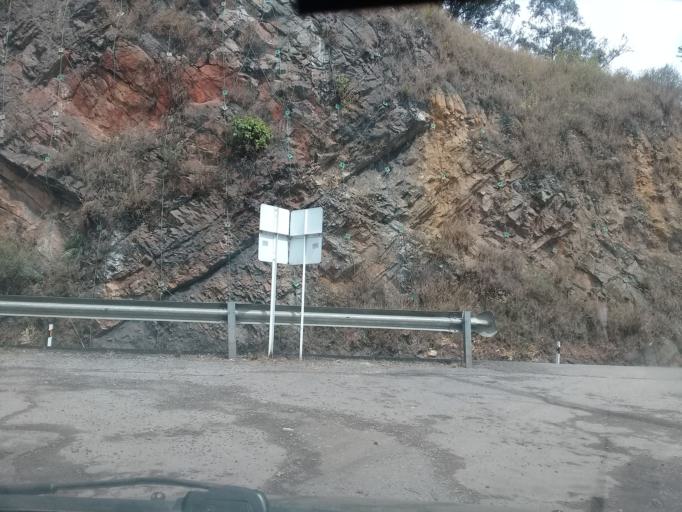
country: CO
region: Cundinamarca
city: Une
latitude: 4.4175
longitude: -73.9867
